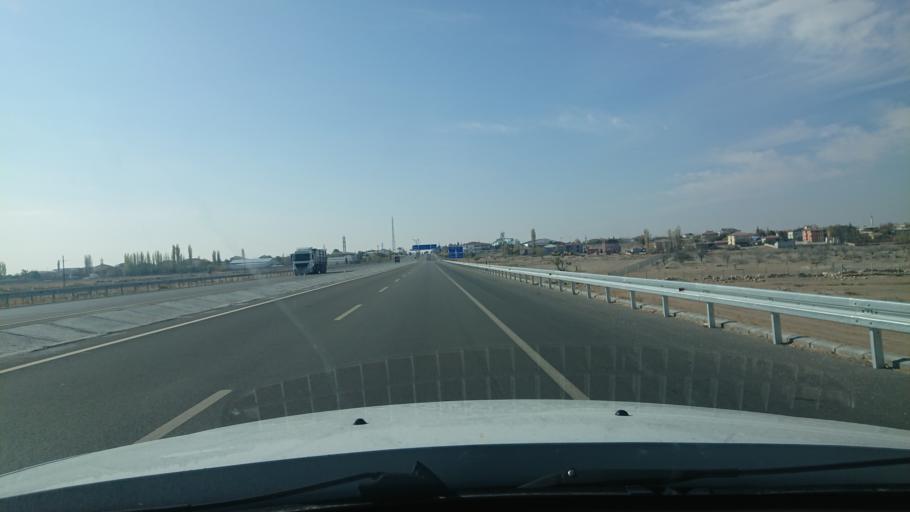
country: TR
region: Aksaray
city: Sultanhani
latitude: 38.2494
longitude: 33.4560
